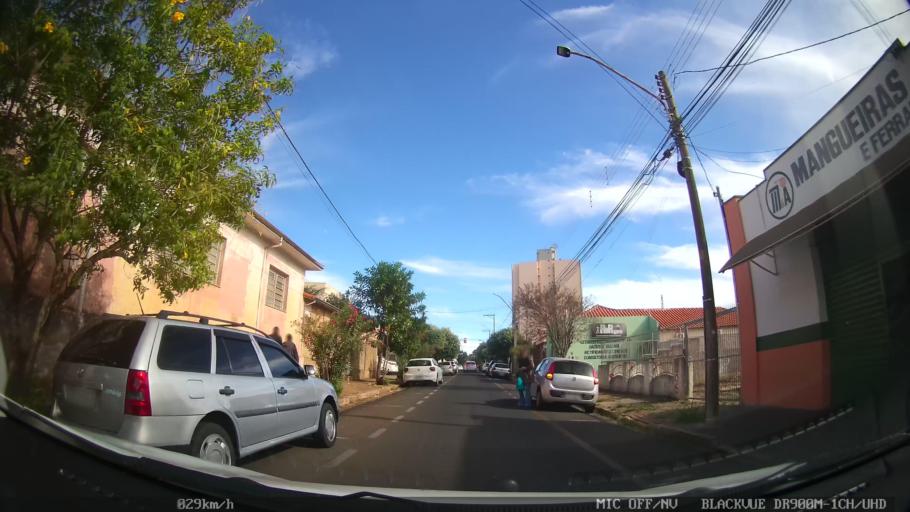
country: BR
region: Sao Paulo
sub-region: Catanduva
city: Catanduva
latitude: -21.1331
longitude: -48.9776
